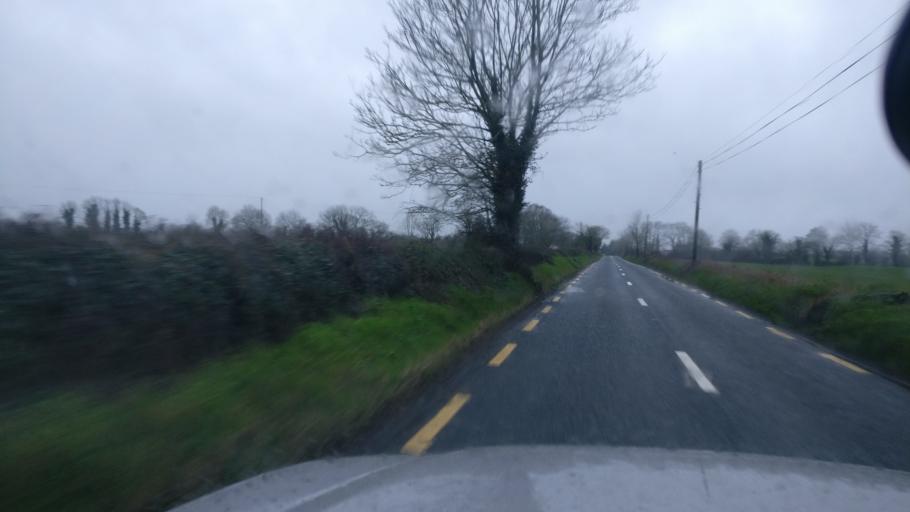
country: IE
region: Connaught
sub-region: County Galway
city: Portumna
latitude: 53.1311
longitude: -8.2061
